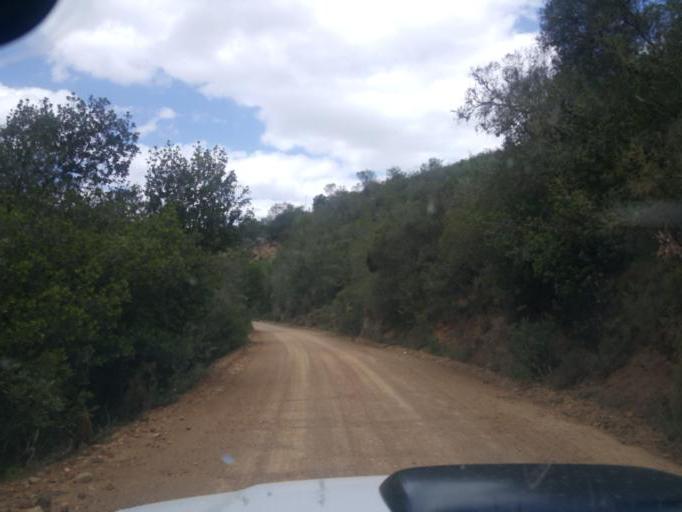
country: ZA
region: Western Cape
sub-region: Eden District Municipality
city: Knysna
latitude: -33.8114
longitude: 23.1690
